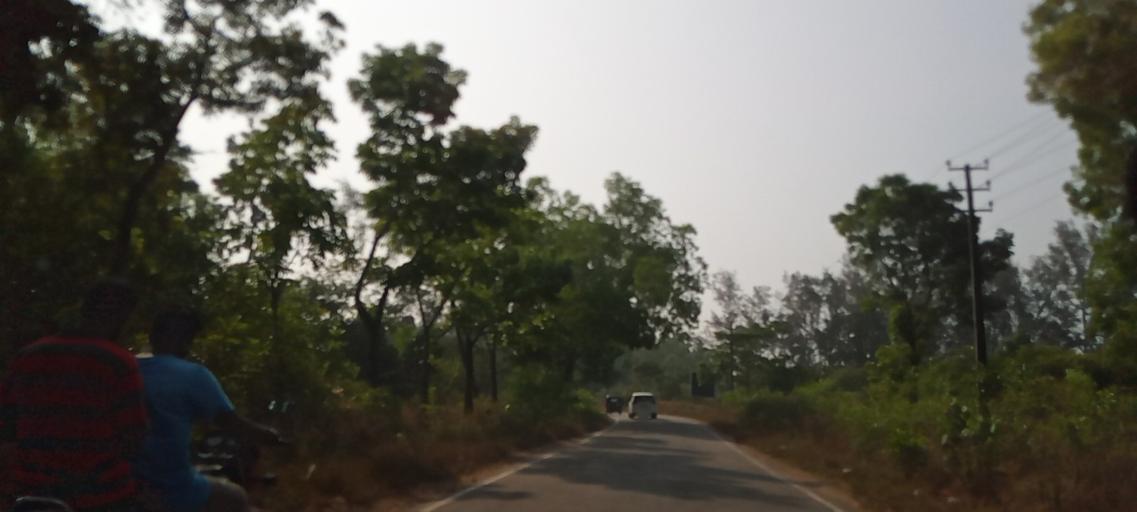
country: IN
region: Karnataka
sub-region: Udupi
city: Coondapoor
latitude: 13.5148
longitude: 74.7703
